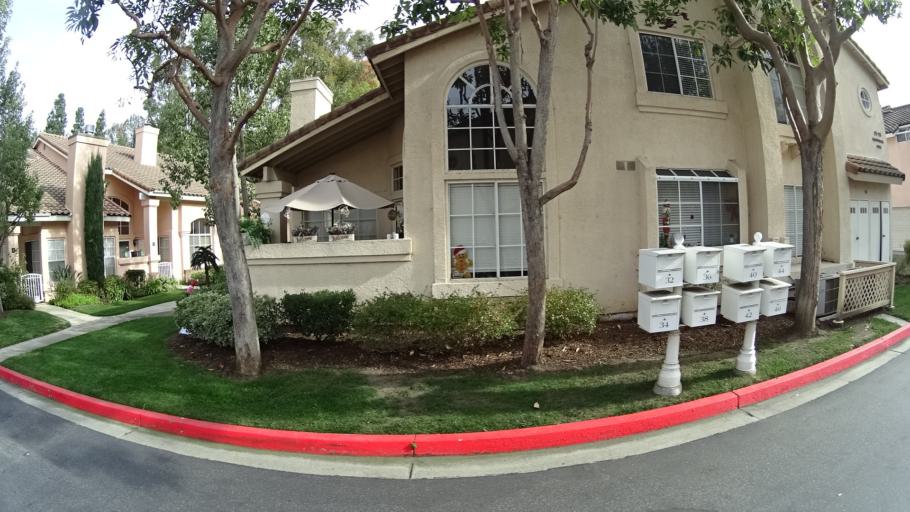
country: US
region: California
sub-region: Orange County
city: Laguna Woods
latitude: 33.6048
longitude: -117.7402
